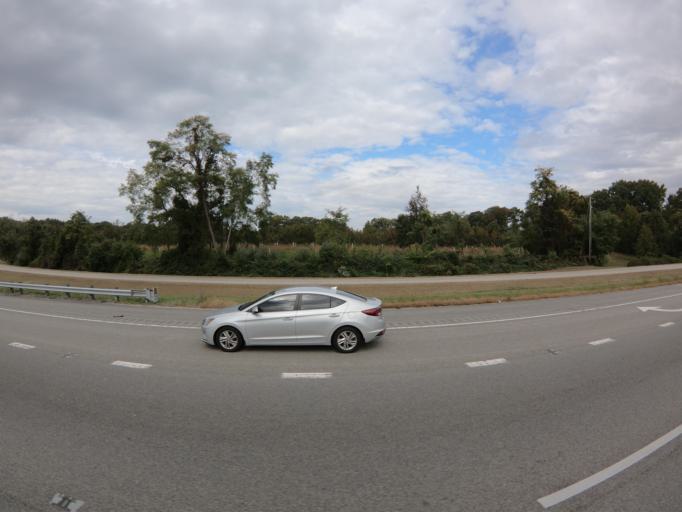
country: US
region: Maryland
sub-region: Queen Anne's County
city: Grasonville
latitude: 38.9696
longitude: -76.1820
